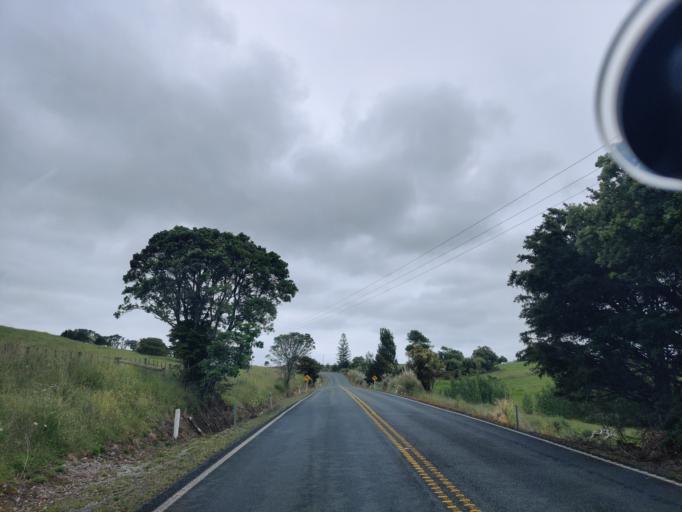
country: NZ
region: Northland
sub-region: Kaipara District
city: Dargaville
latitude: -36.1262
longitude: 174.1163
